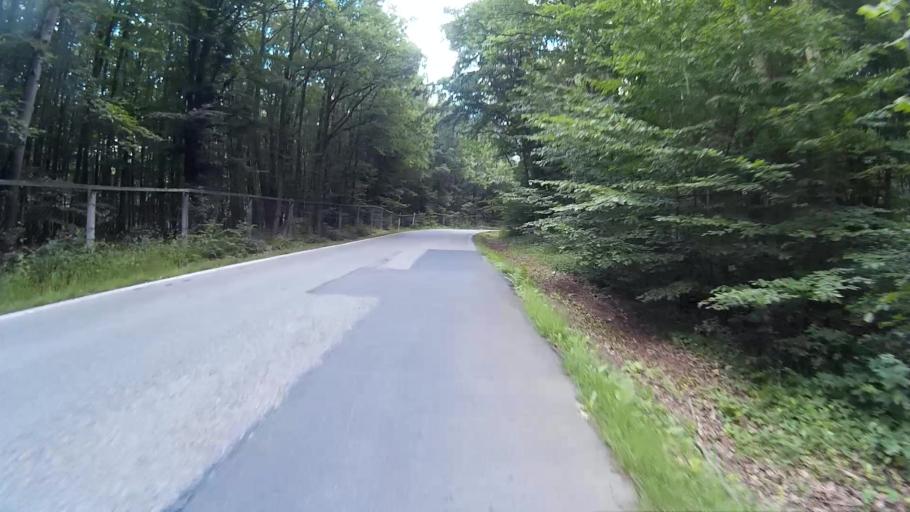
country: CZ
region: South Moravian
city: Ricany
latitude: 49.2078
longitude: 16.4461
